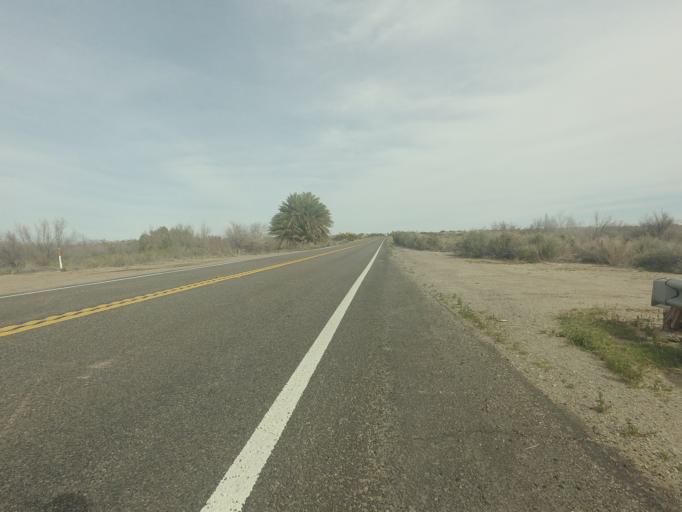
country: US
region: California
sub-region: Imperial County
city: Holtville
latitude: 32.9748
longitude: -115.2998
